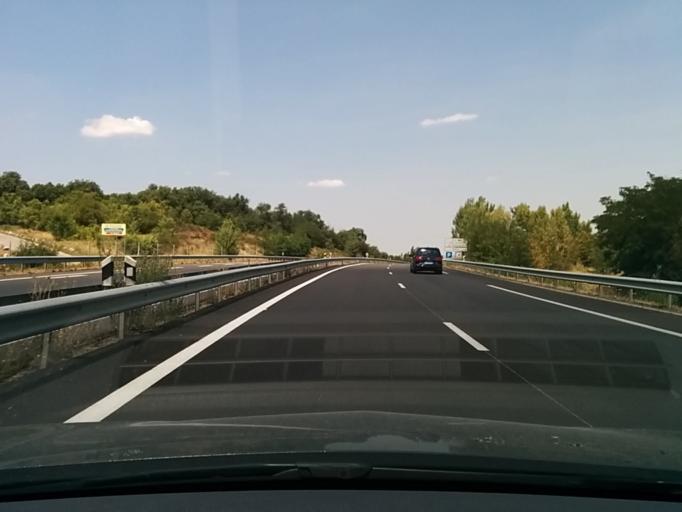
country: FR
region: Midi-Pyrenees
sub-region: Departement du Gers
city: Pujaudran
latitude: 43.5837
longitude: 1.1279
